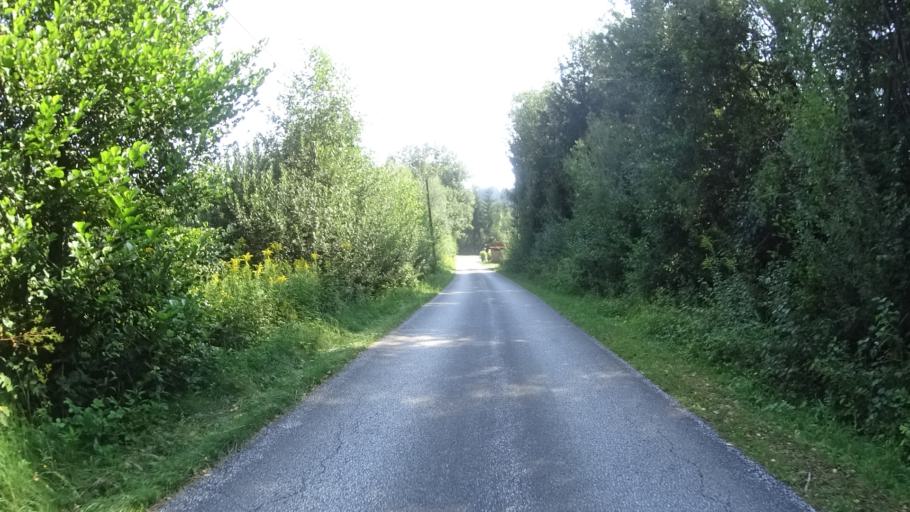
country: AT
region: Carinthia
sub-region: Politischer Bezirk Volkermarkt
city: Gallizien
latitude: 46.5644
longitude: 14.5001
